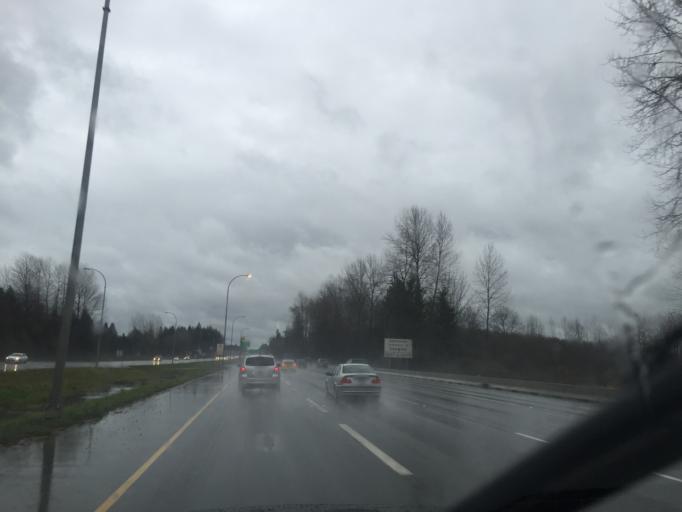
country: CA
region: British Columbia
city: Walnut Grove
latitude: 49.1688
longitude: -122.6868
